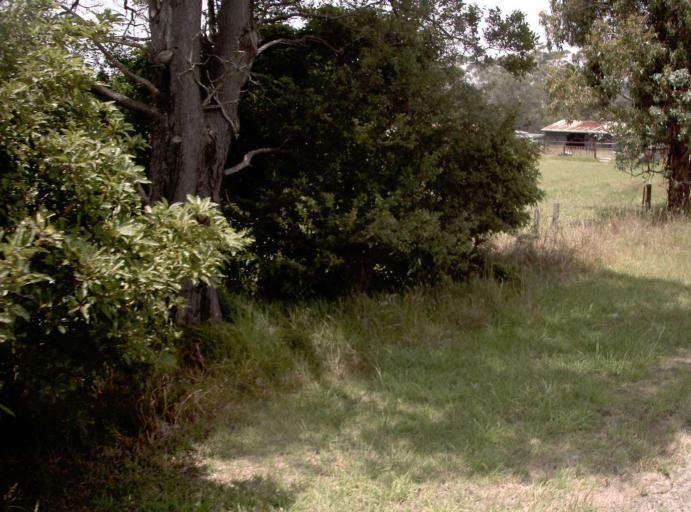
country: AU
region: Victoria
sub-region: Latrobe
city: Traralgon
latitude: -38.3750
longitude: 146.7543
